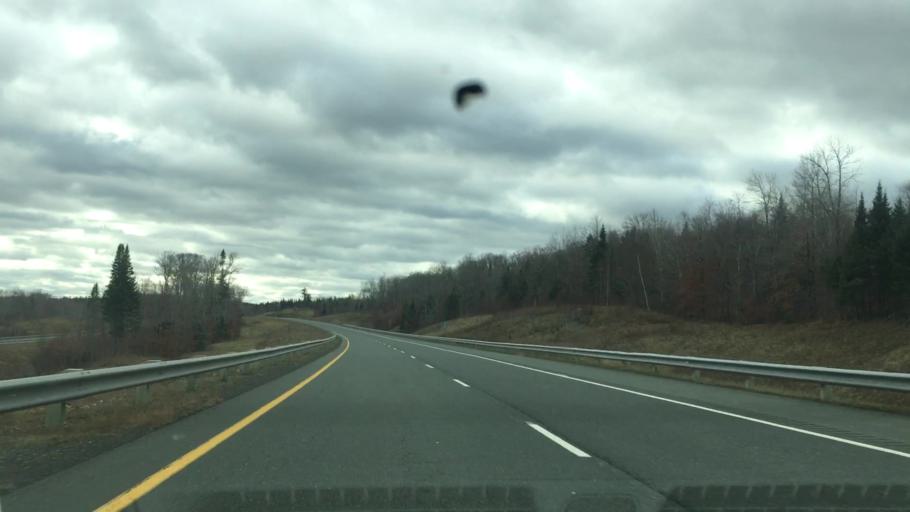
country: US
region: Maine
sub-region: Aroostook County
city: Fort Fairfield
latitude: 46.6476
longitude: -67.7433
